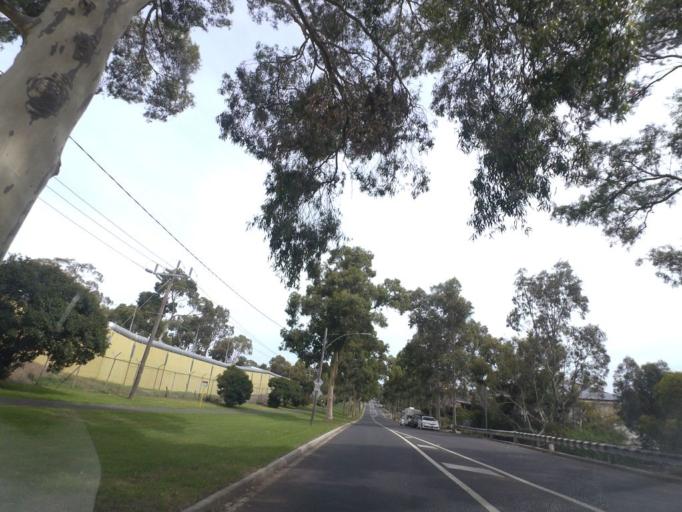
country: AU
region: Victoria
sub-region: Moonee Valley
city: Travancore
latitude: -37.7762
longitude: 144.9430
